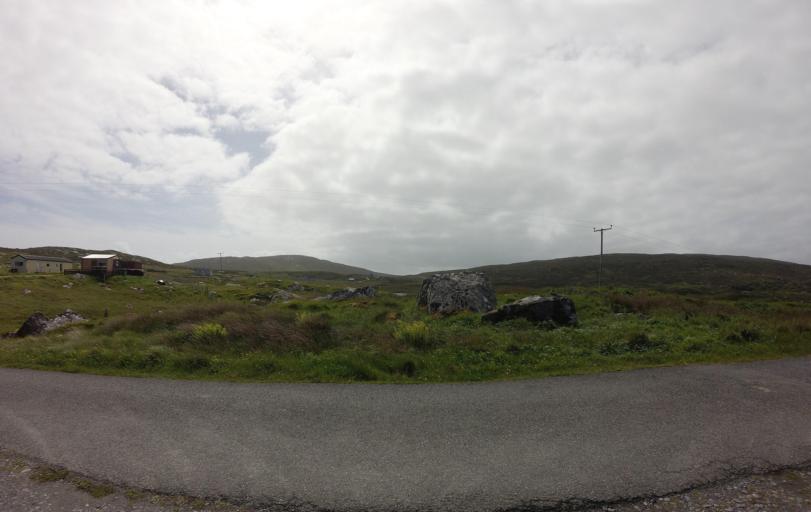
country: GB
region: Scotland
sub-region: Eilean Siar
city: Isle of South Uist
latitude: 57.1366
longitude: -7.3079
